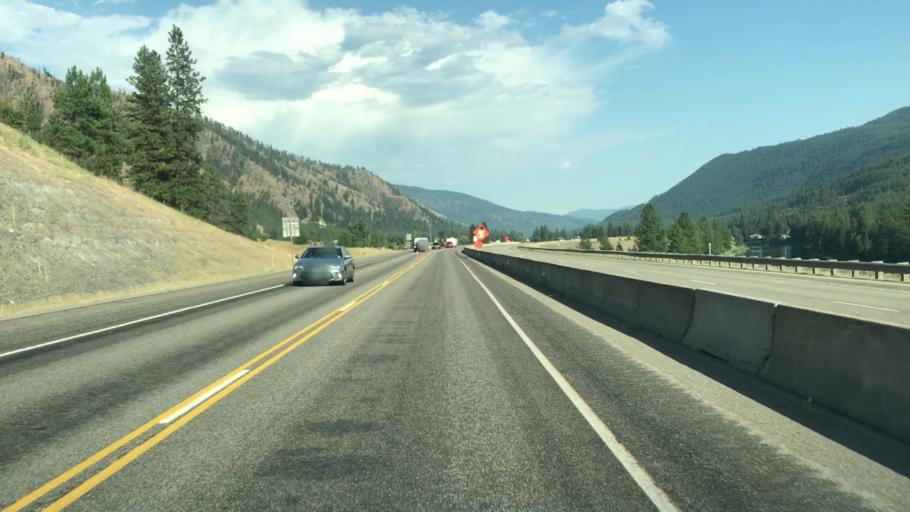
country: US
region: Montana
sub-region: Mineral County
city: Superior
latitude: 47.2158
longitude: -114.9475
